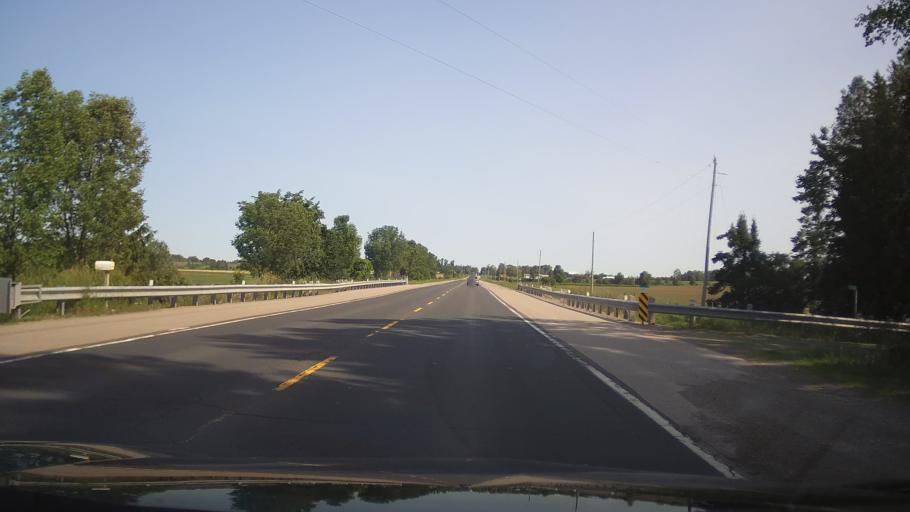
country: CA
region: Ontario
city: Omemee
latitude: 44.3204
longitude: -78.6828
